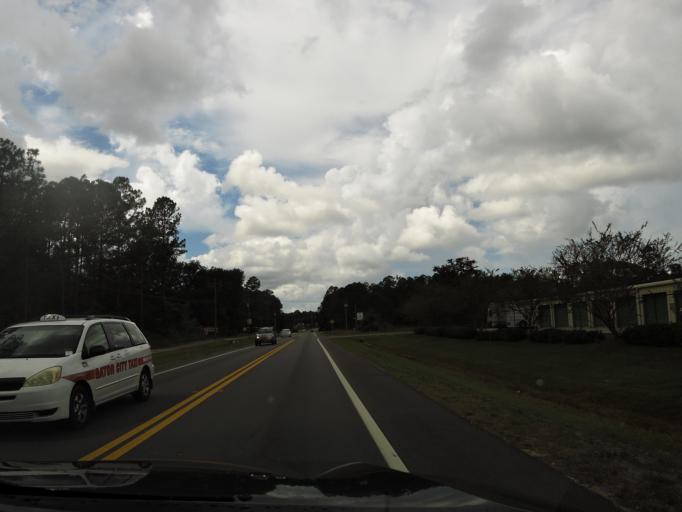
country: US
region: Florida
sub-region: Clay County
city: Middleburg
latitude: 30.0628
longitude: -81.9025
